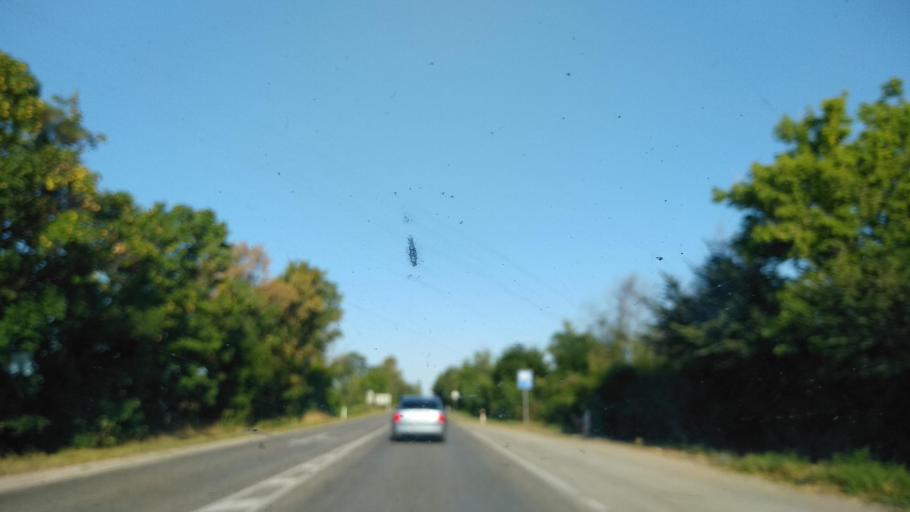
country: BG
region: Gabrovo
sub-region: Obshtina Dryanovo
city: Dryanovo
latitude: 43.0880
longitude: 25.4619
